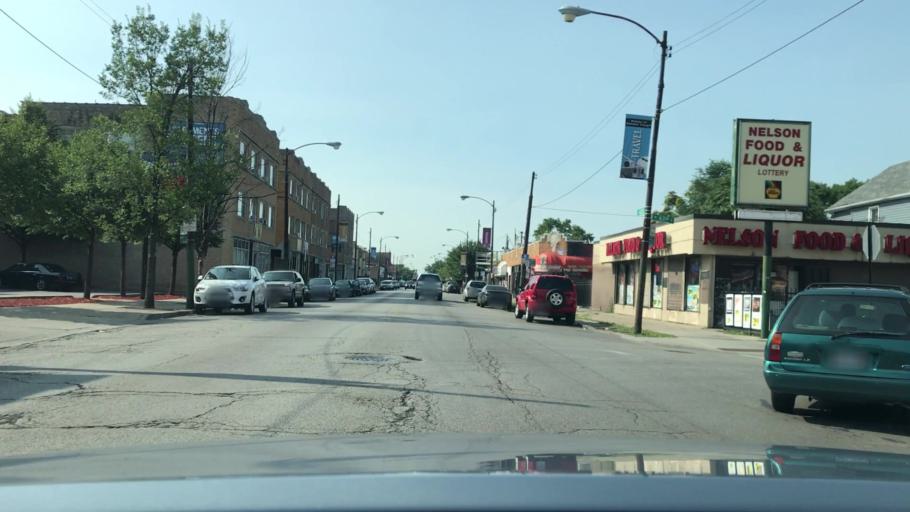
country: US
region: Illinois
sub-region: Cook County
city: Hometown
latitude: 41.7782
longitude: -87.7031
